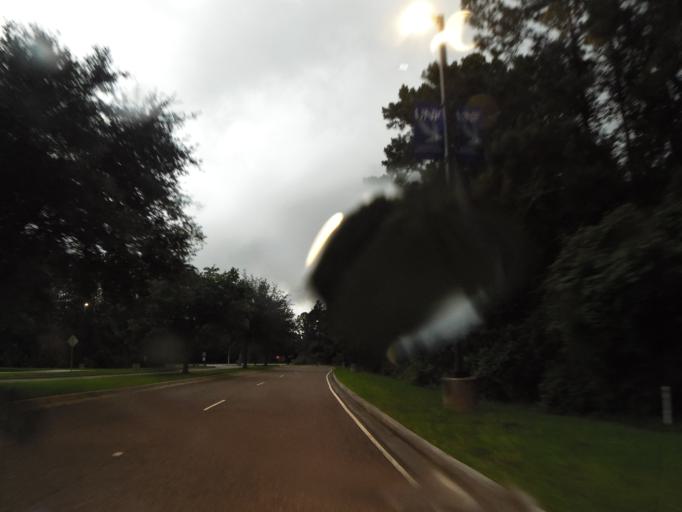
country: US
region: Florida
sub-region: Duval County
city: Neptune Beach
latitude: 30.2810
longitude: -81.5103
